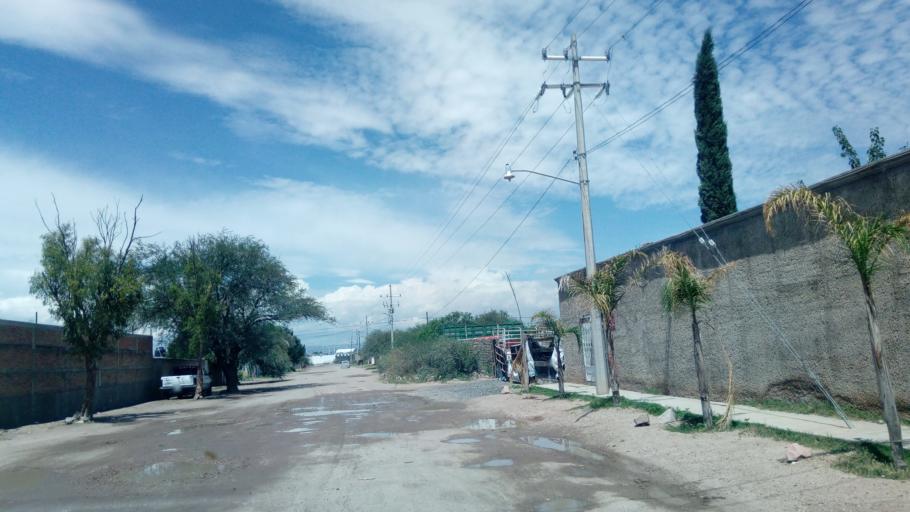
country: MX
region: Durango
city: Victoria de Durango
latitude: 24.0167
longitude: -104.5900
